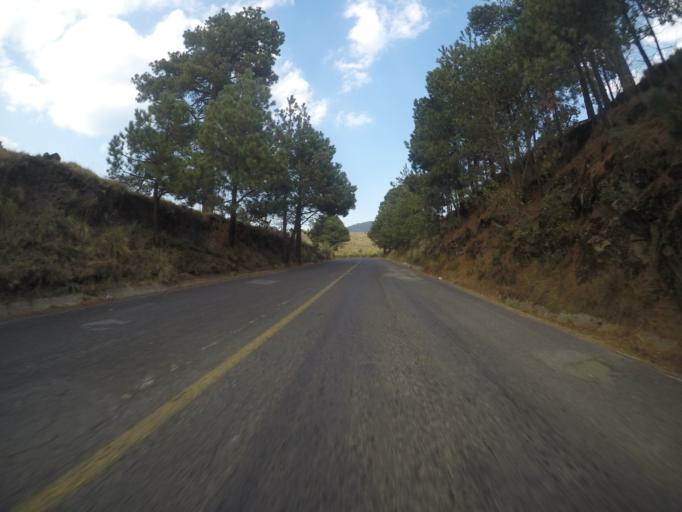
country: MX
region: Mexico
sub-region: Xalatlaco
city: San Juan Tomasquillo Herradura
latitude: 19.1843
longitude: -99.3534
